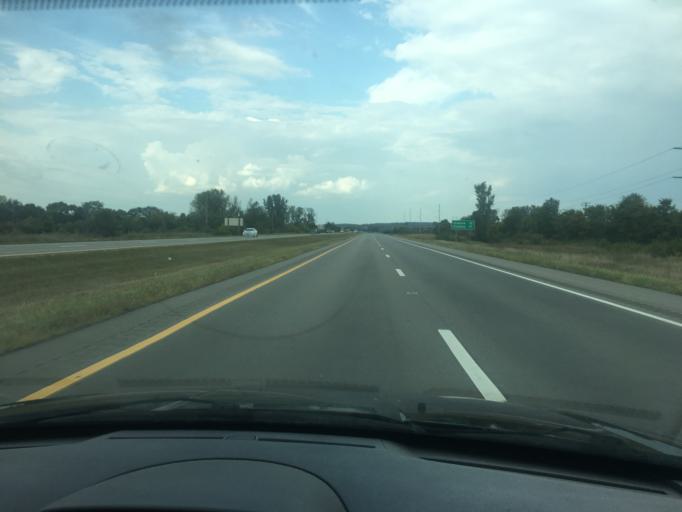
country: US
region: Ohio
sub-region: Clark County
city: Springfield
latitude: 39.9536
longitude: -83.8309
